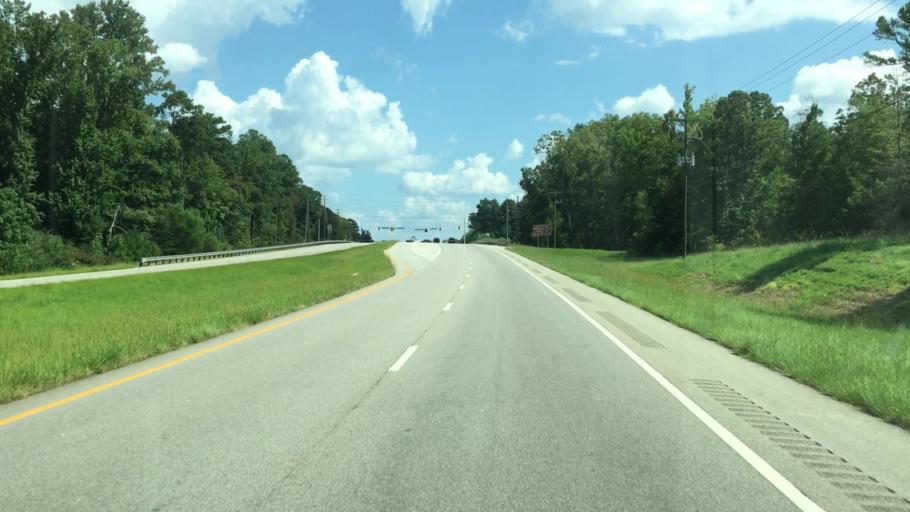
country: US
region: Georgia
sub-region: Putnam County
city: Eatonton
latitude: 33.2397
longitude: -83.3212
